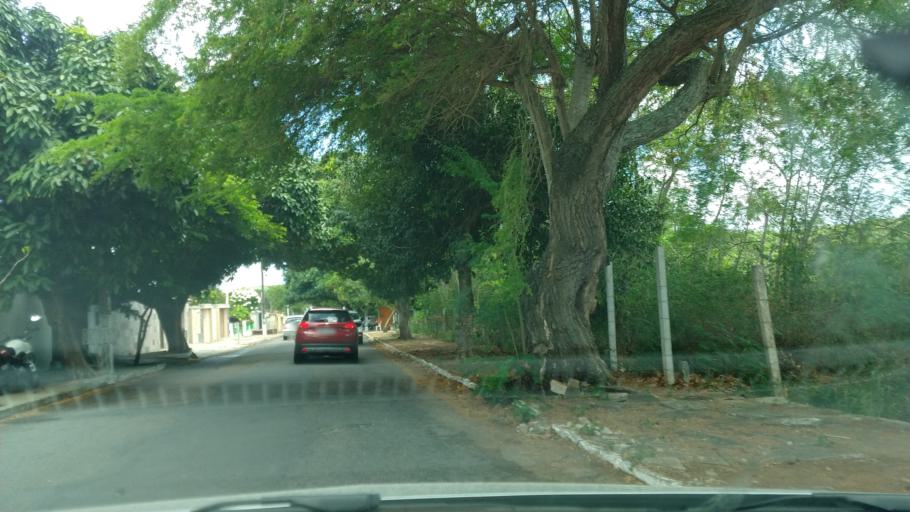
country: BR
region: Rio Grande do Norte
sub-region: Natal
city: Natal
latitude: -5.8506
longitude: -35.1984
